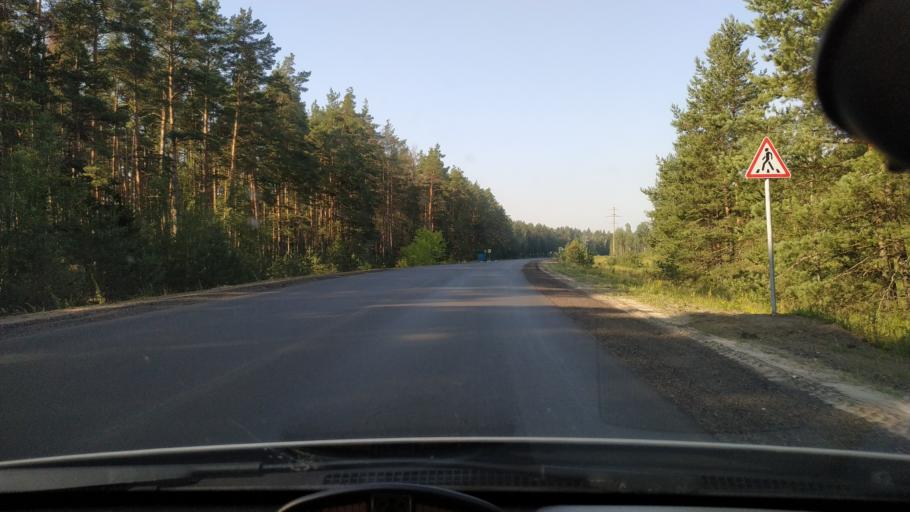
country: RU
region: Moskovskaya
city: Kerva
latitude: 55.5712
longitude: 39.6741
